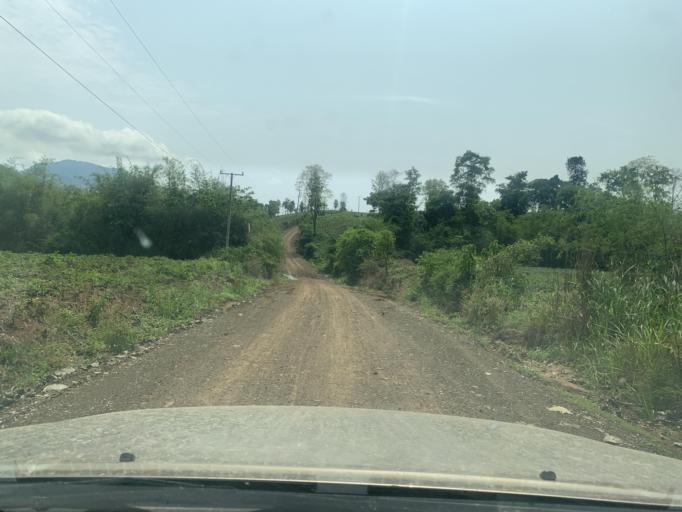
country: TH
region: Uttaradit
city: Ban Khok
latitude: 18.3566
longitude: 101.3820
